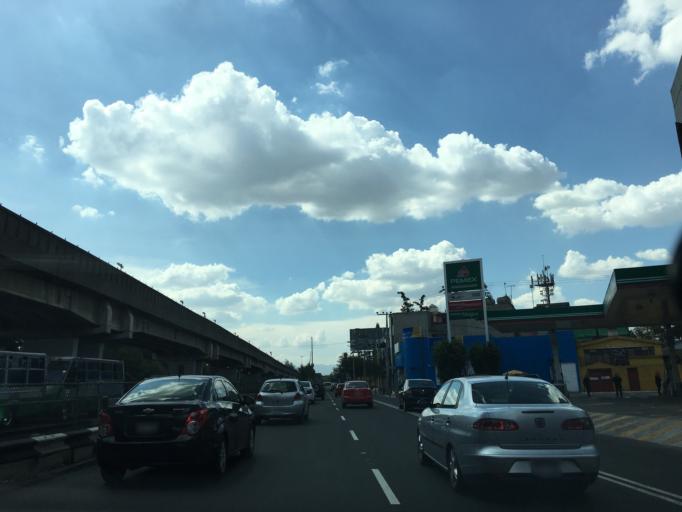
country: MX
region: Mexico City
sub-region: Iztacalco
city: Iztacalco
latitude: 19.4075
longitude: -99.0828
